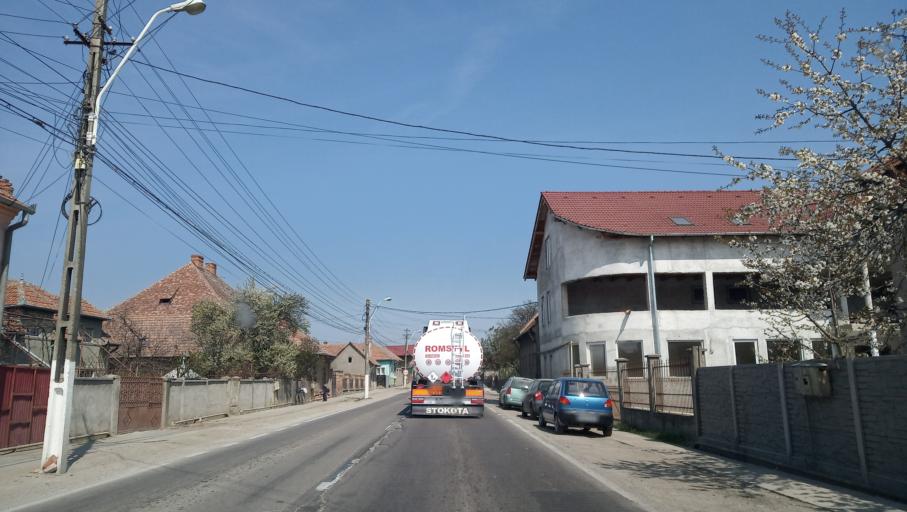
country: RO
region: Alba
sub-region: Oras Teius
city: Teius
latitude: 46.2088
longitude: 23.6755
